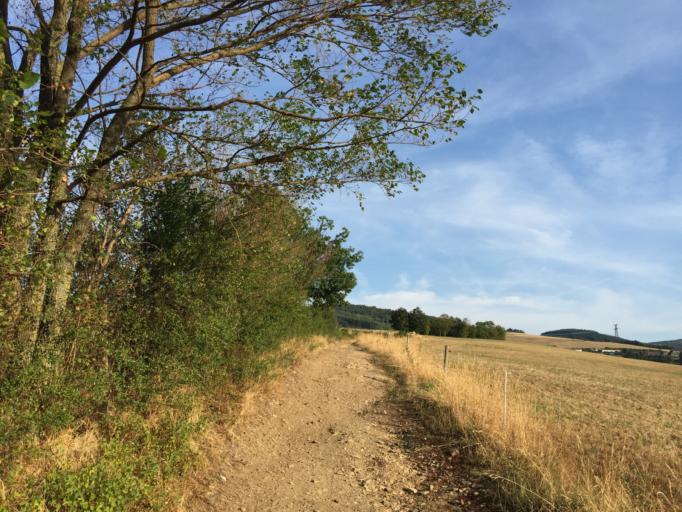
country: FR
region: Rhone-Alpes
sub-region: Departement de la Loire
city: Saint-Paul-en-Jarez
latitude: 45.4792
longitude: 4.5565
